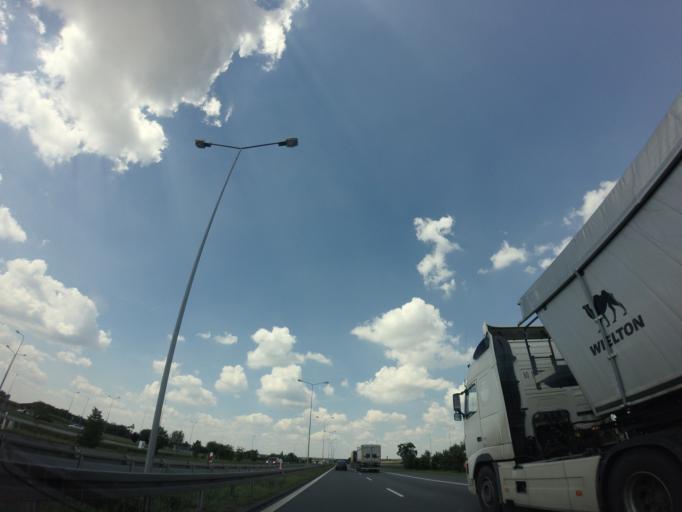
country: PL
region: Opole Voivodeship
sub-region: Powiat opolski
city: Proszkow
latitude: 50.5693
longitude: 17.8604
